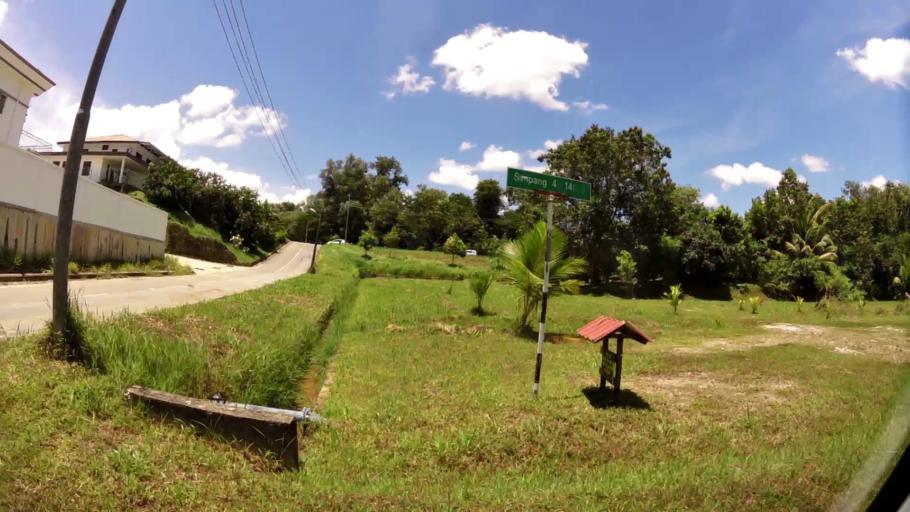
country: BN
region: Brunei and Muara
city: Bandar Seri Begawan
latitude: 4.9363
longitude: 114.9644
